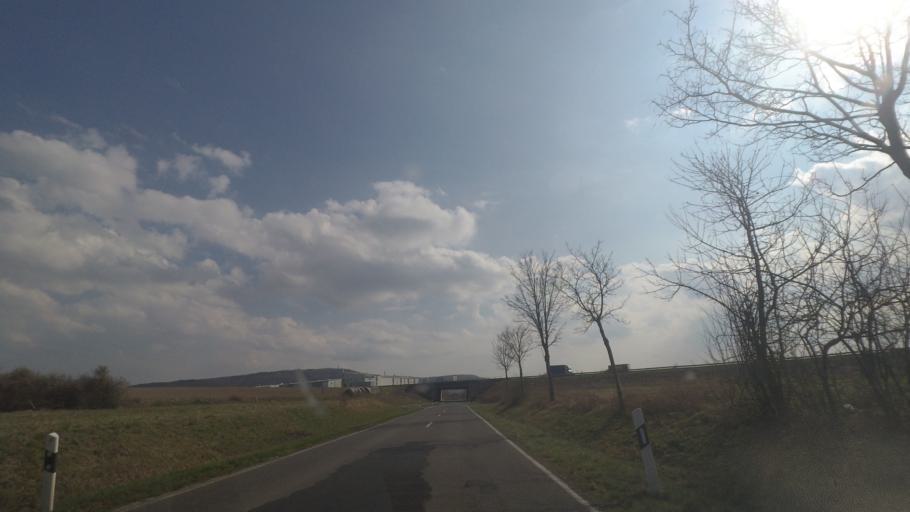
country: DE
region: Bavaria
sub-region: Regierungsbezirk Unterfranken
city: Wiesentheid
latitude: 49.7755
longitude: 10.3632
